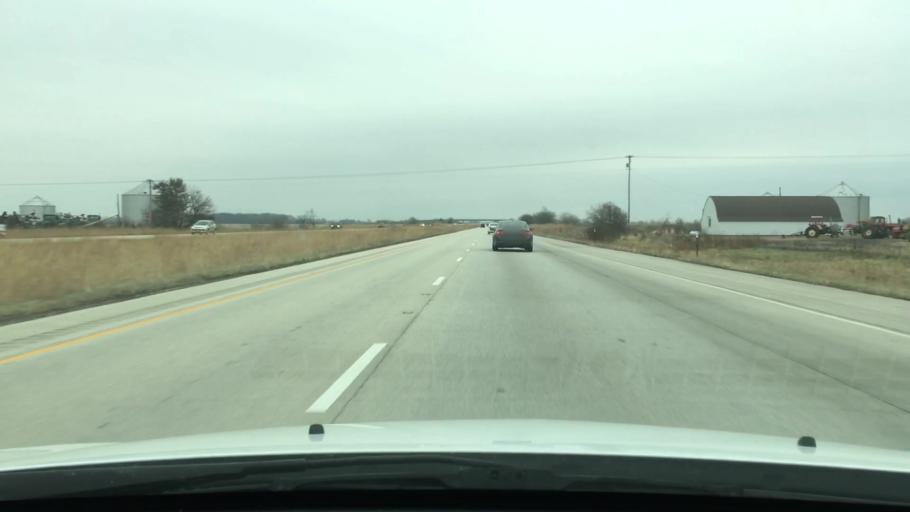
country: US
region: Illinois
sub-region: Sangamon County
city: New Berlin
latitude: 39.7401
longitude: -89.9166
